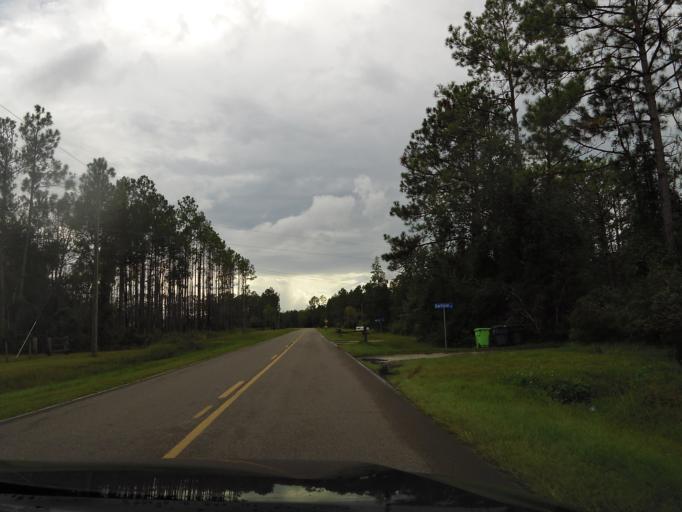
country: US
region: Florida
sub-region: Duval County
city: Baldwin
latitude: 30.4269
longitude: -82.0214
